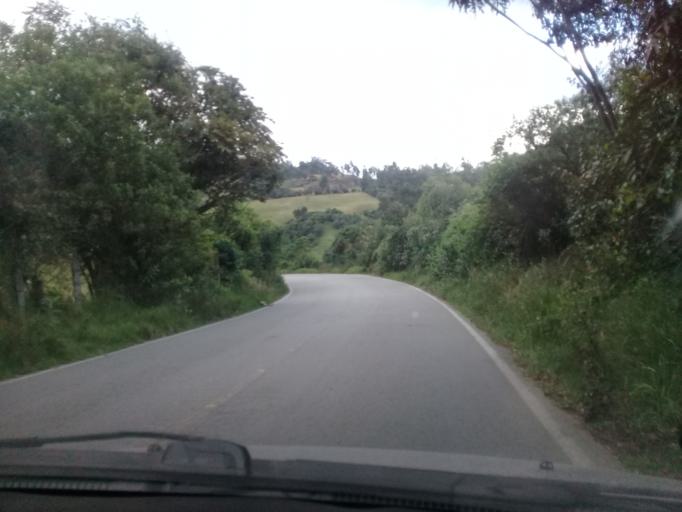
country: CO
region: Cundinamarca
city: Tabio
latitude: 4.9425
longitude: -74.1092
